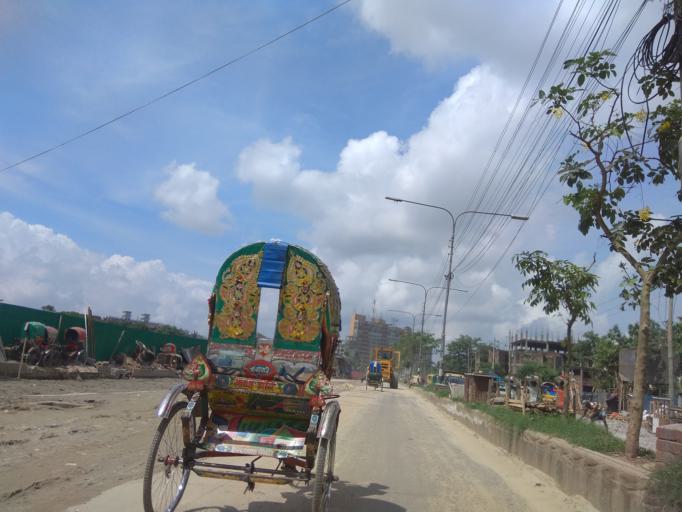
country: BD
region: Dhaka
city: Paltan
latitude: 23.8075
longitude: 90.3897
